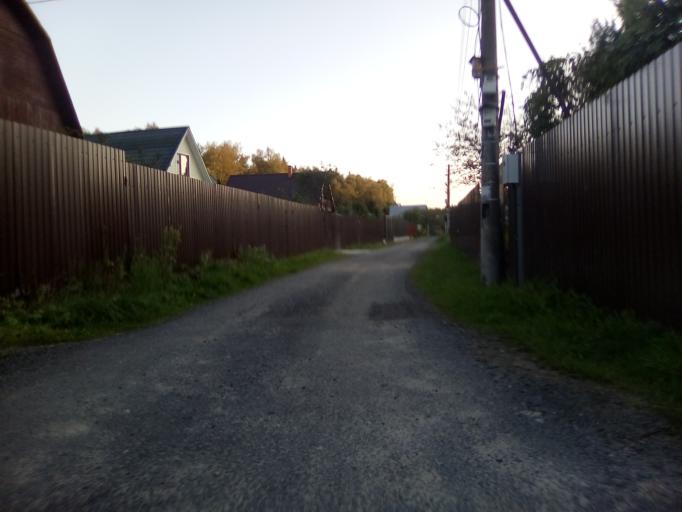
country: RU
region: Moskovskaya
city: Krasnoznamensk
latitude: 55.5614
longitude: 37.0280
